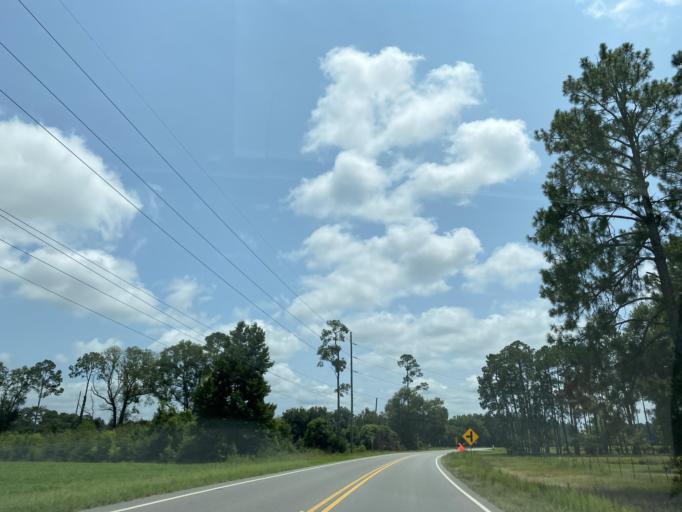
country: US
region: Georgia
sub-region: Jeff Davis County
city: Hazlehurst
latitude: 31.8220
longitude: -82.5686
